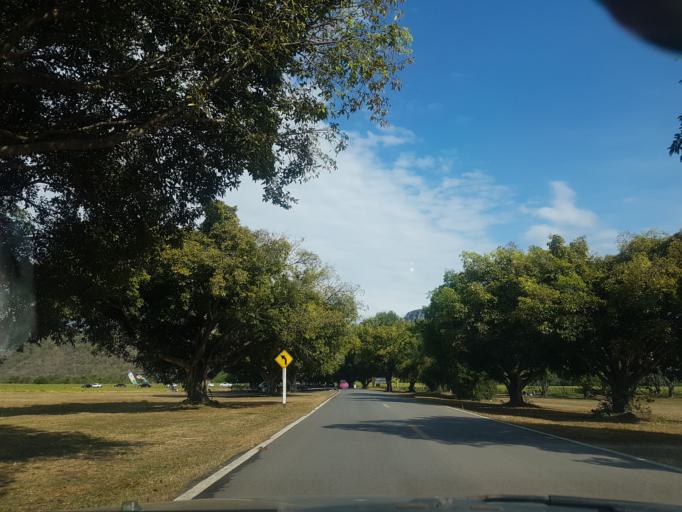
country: TH
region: Sara Buri
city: Phra Phutthabat
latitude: 14.8125
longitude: 100.7519
